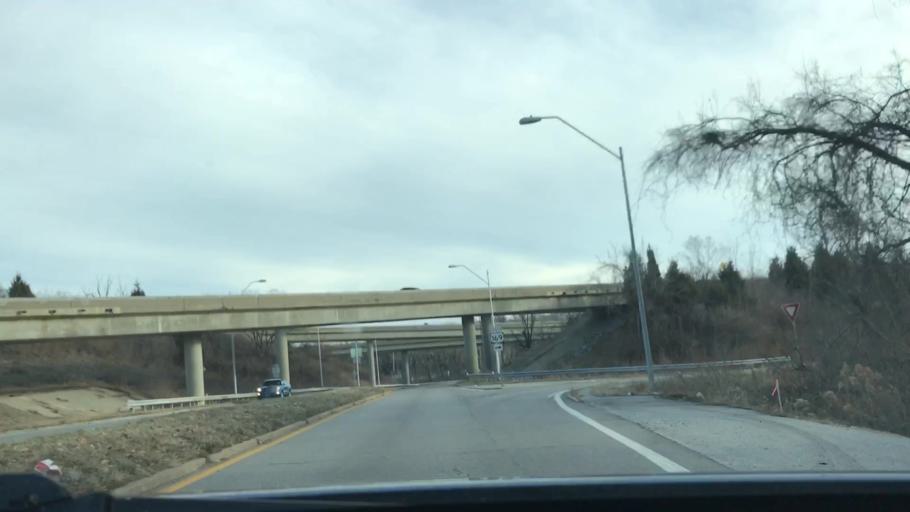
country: US
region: Missouri
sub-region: Platte County
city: Riverside
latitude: 39.1822
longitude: -94.5948
